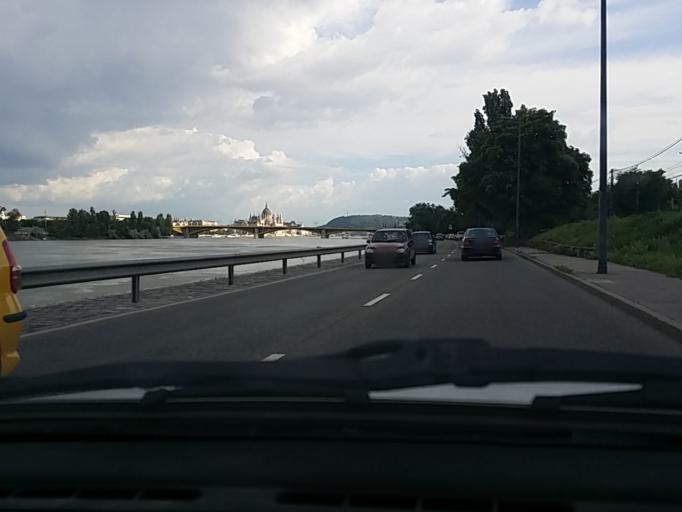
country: HU
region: Budapest
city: Budapest II. keruelet
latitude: 47.5218
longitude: 19.0387
